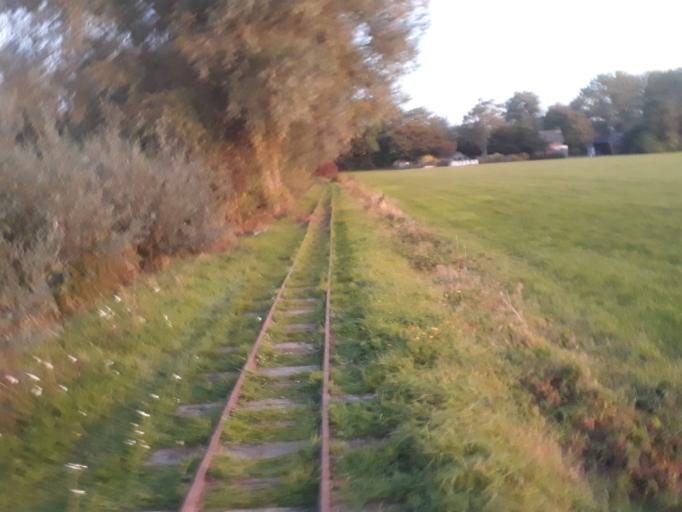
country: NL
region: Gelderland
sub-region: Gemeente Zevenaar
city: Zevenaar
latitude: 51.9172
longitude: 6.0715
